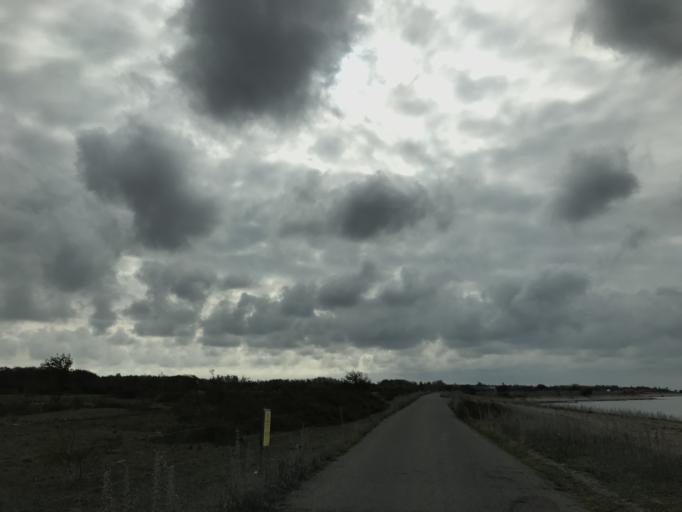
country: SE
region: Kalmar
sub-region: Borgholms Kommun
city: Borgholm
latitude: 57.0522
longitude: 16.8363
